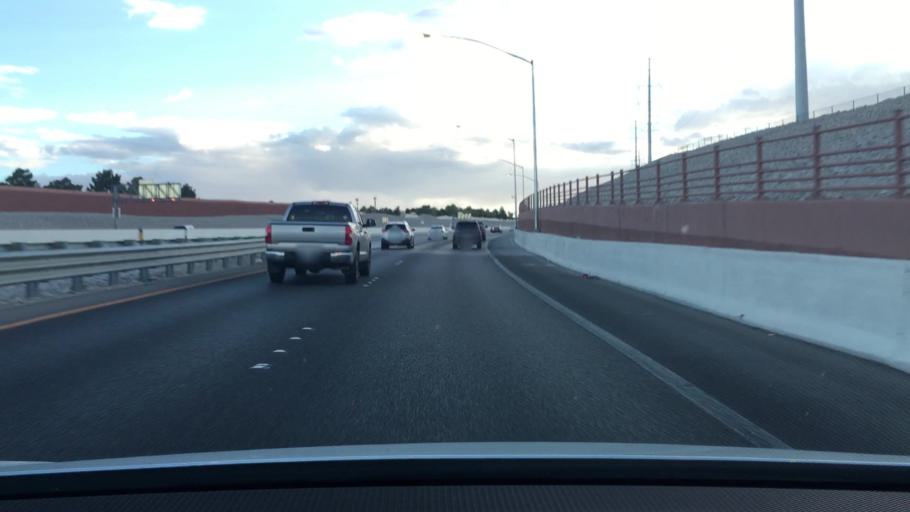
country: US
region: Nevada
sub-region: Clark County
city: Summerlin South
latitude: 36.2164
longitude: -115.3310
